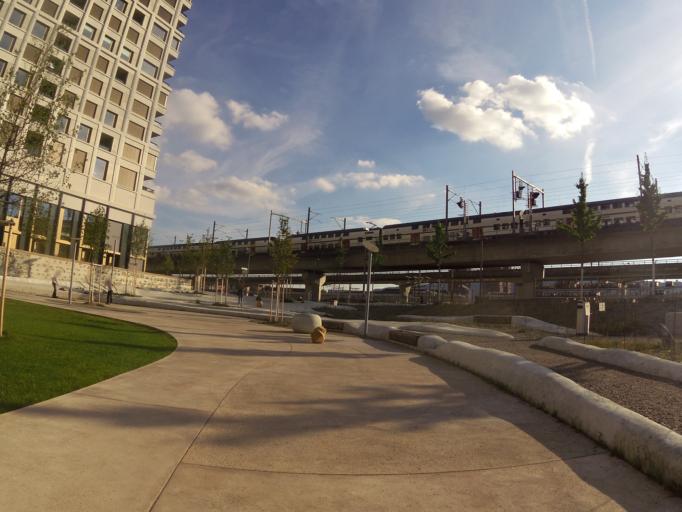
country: CH
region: Zurich
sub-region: Bezirk Zuerich
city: Zuerich (Kreis 5) / Escher-Wyss
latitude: 47.3876
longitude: 8.5124
